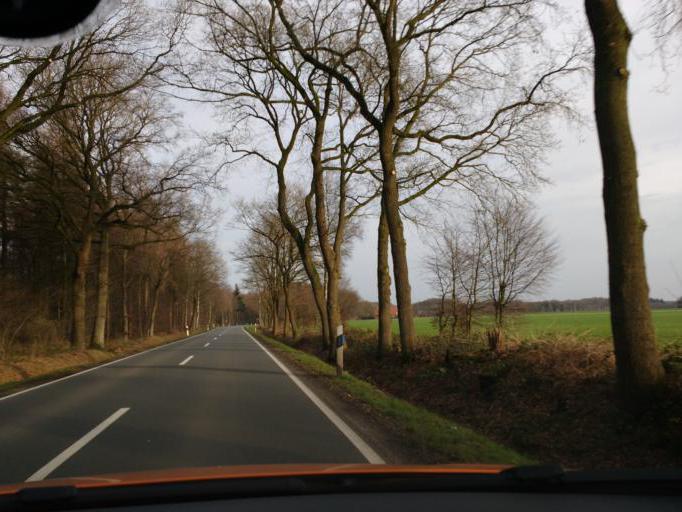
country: DE
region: Lower Saxony
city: Hude
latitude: 53.0547
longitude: 8.4548
